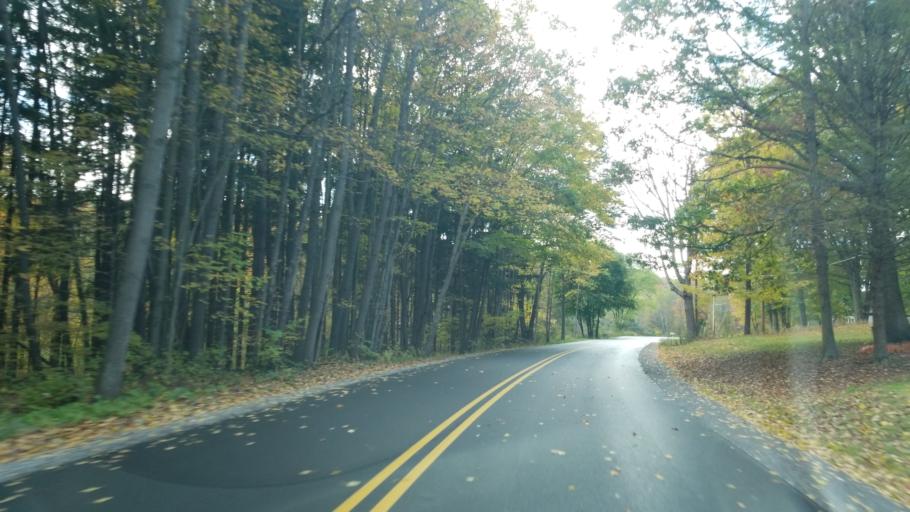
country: US
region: Pennsylvania
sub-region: Clearfield County
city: Sandy
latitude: 41.0889
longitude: -78.7945
